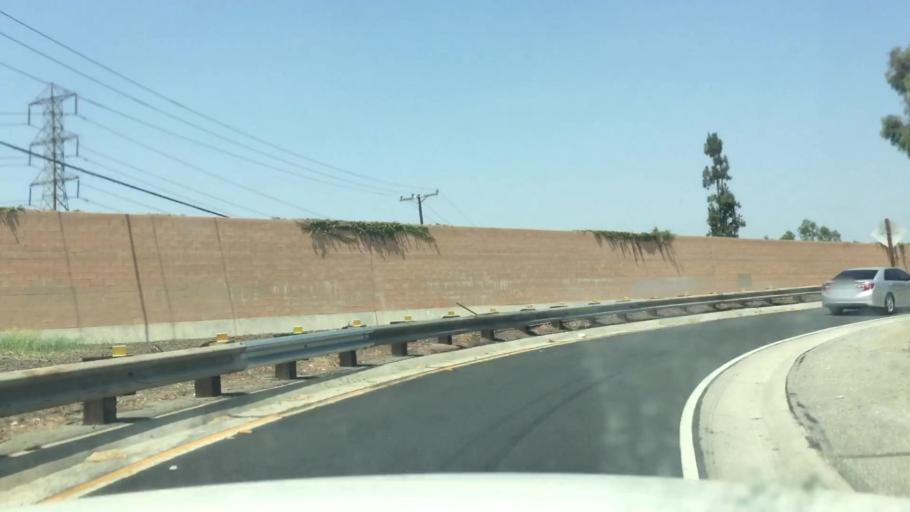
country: US
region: California
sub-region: Los Angeles County
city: West Whittier-Los Nietos
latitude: 33.9748
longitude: -118.0812
